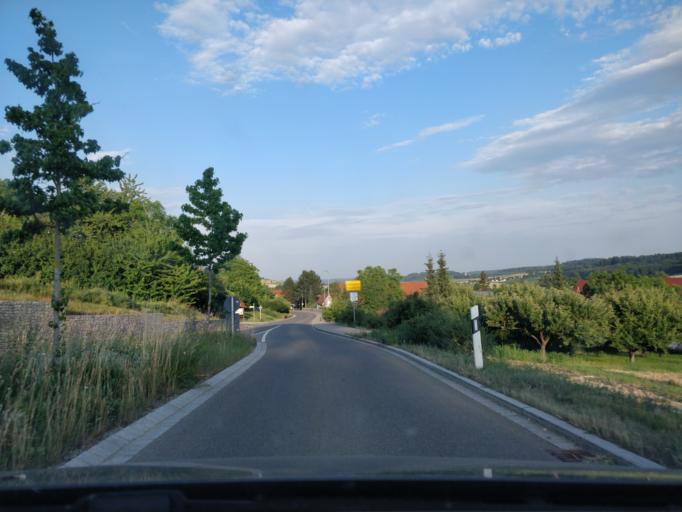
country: DE
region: Bavaria
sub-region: Swabia
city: Ederheim
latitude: 48.8100
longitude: 10.4584
